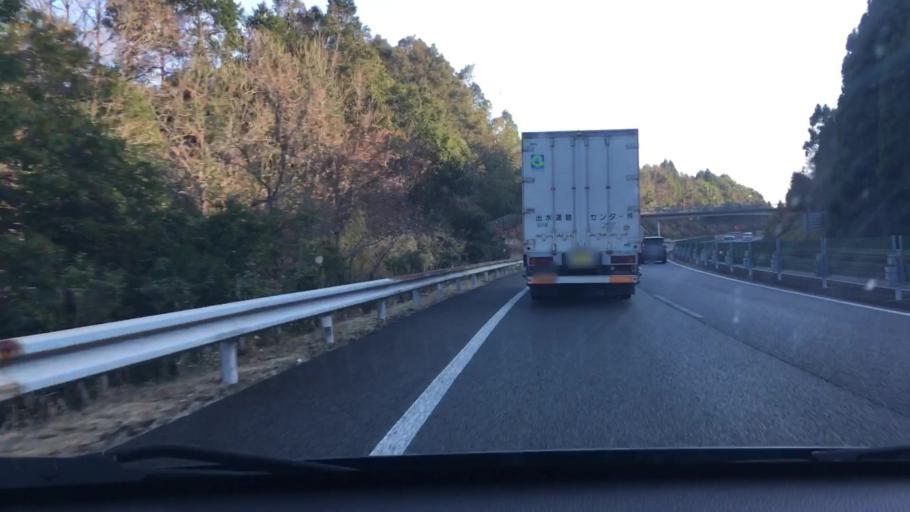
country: JP
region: Kagoshima
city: Kajiki
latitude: 31.8305
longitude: 130.6934
